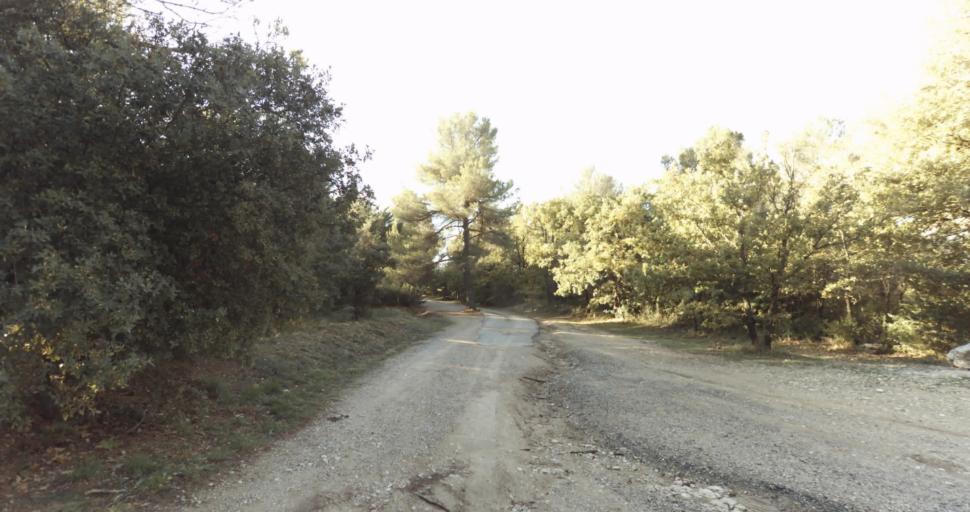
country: FR
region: Provence-Alpes-Cote d'Azur
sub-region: Departement des Bouches-du-Rhone
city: Venelles
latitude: 43.6057
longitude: 5.4727
